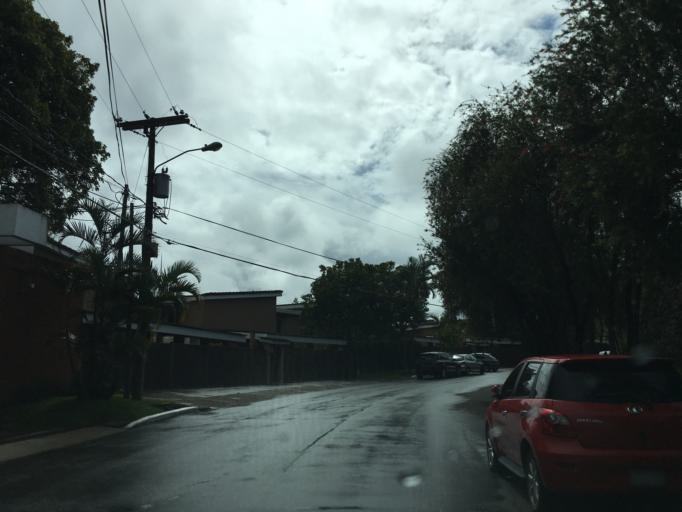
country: GT
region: Guatemala
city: Santa Catarina Pinula
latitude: 14.5825
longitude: -90.4888
